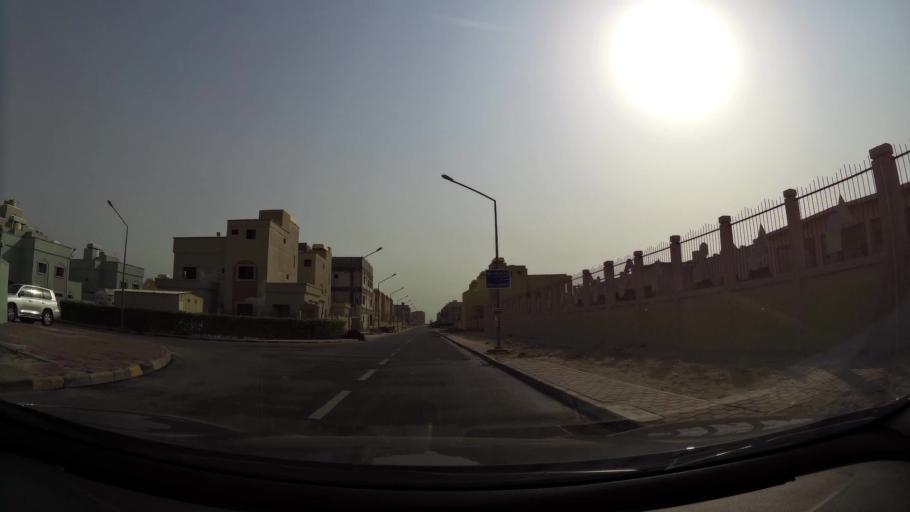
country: KW
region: Al Asimah
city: Ar Rabiyah
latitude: 29.3334
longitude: 47.8043
